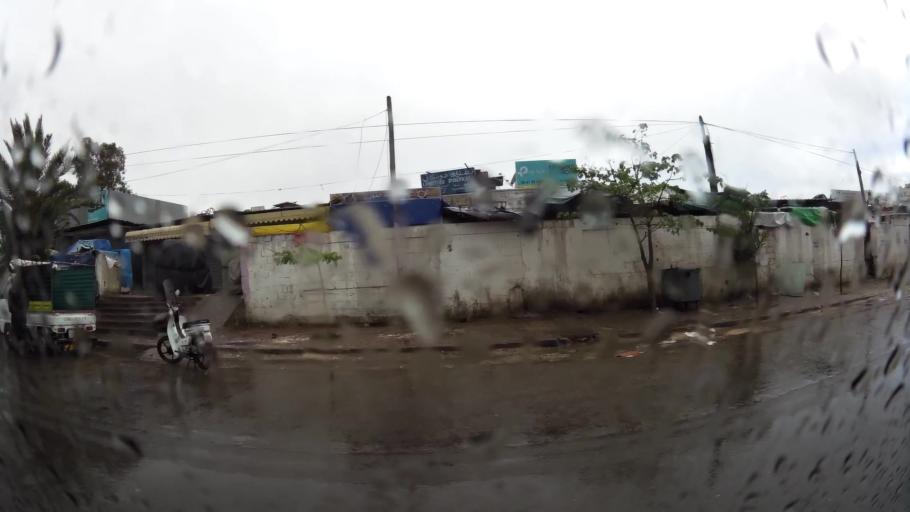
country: MA
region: Grand Casablanca
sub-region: Casablanca
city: Casablanca
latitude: 33.5707
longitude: -7.6288
